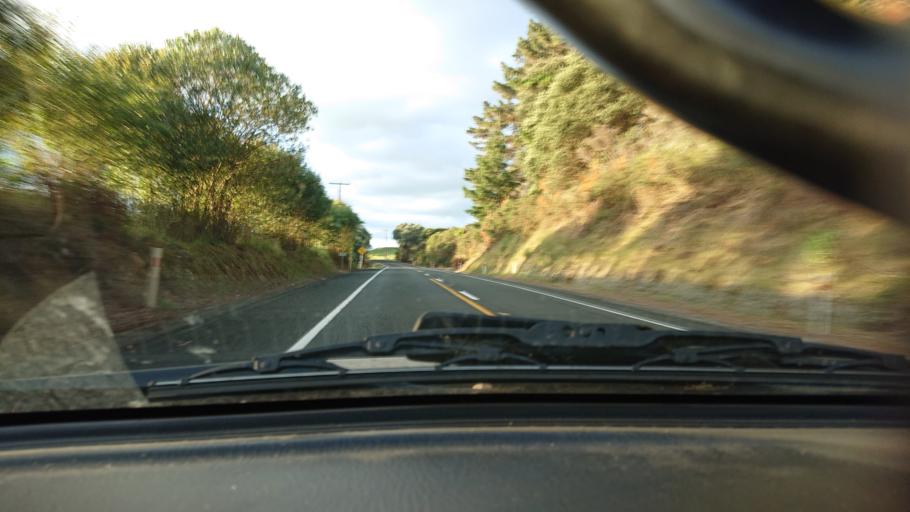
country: NZ
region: Auckland
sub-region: Auckland
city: Parakai
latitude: -36.5019
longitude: 174.4541
